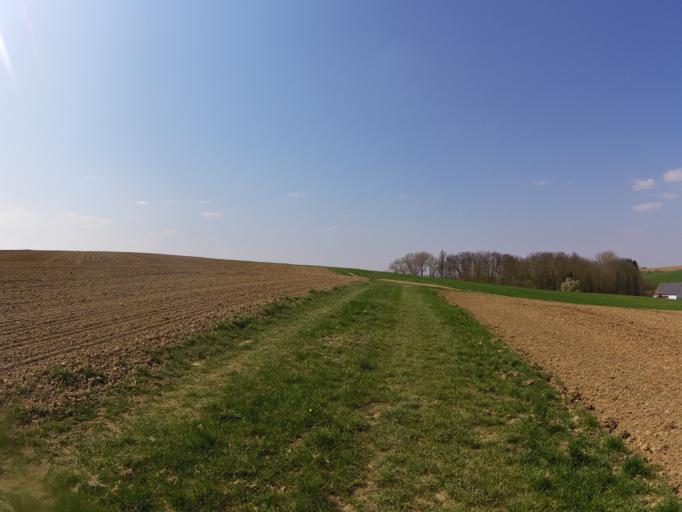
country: DE
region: Bavaria
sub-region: Regierungsbezirk Unterfranken
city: Dettelbach
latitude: 49.8192
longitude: 10.1422
